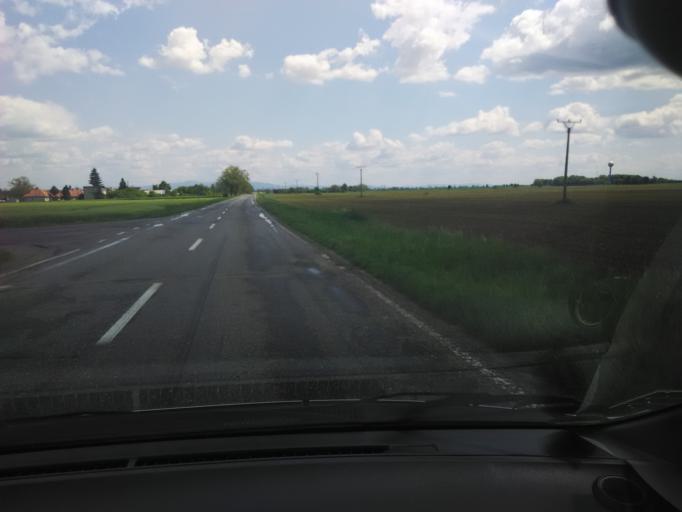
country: SK
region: Nitriansky
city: Levice
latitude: 48.1684
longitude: 18.5440
